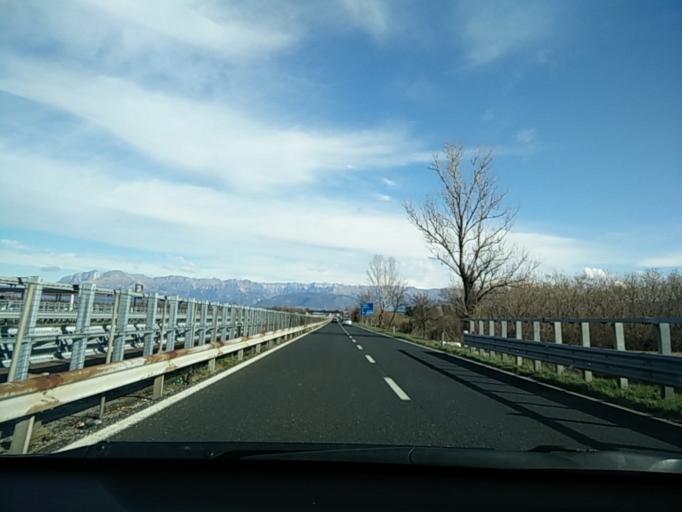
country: IT
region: Friuli Venezia Giulia
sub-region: Provincia di Udine
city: Colugna
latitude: 46.0958
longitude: 13.1978
